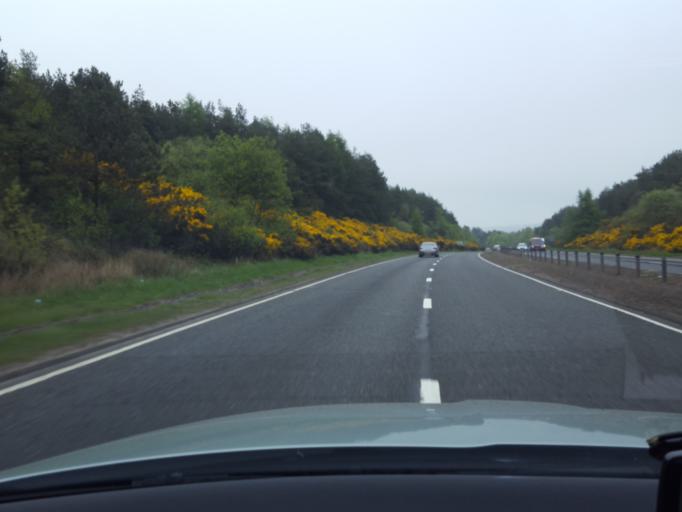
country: GB
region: Scotland
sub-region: Dundee City
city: Dundee
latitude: 56.5535
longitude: -2.9337
